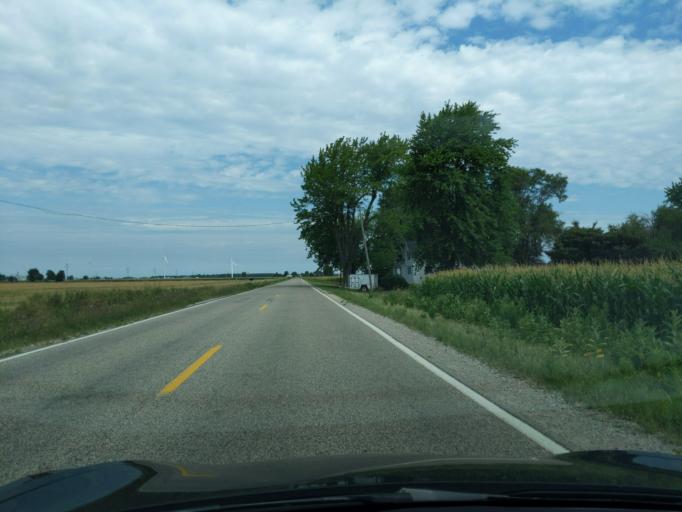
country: US
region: Michigan
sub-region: Gratiot County
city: Breckenridge
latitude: 43.3673
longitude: -84.4298
